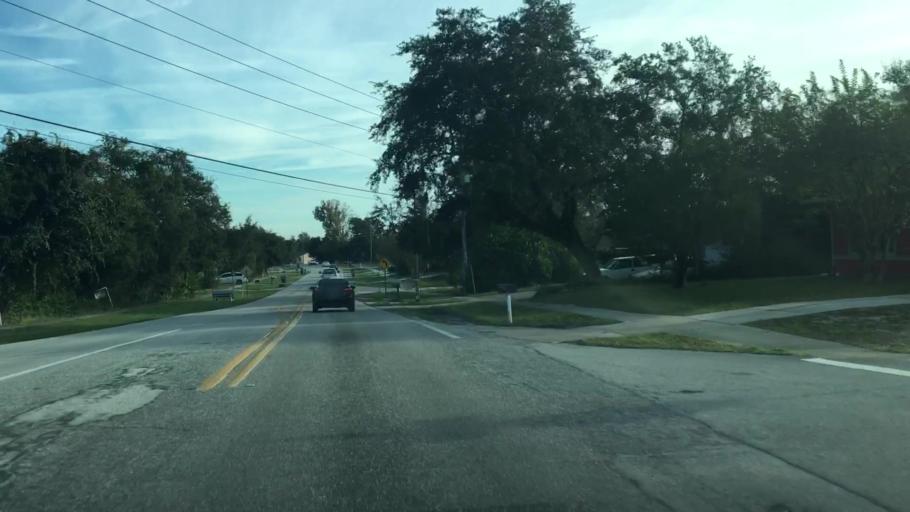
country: US
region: Florida
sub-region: Volusia County
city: Deltona
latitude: 28.9083
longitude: -81.2238
